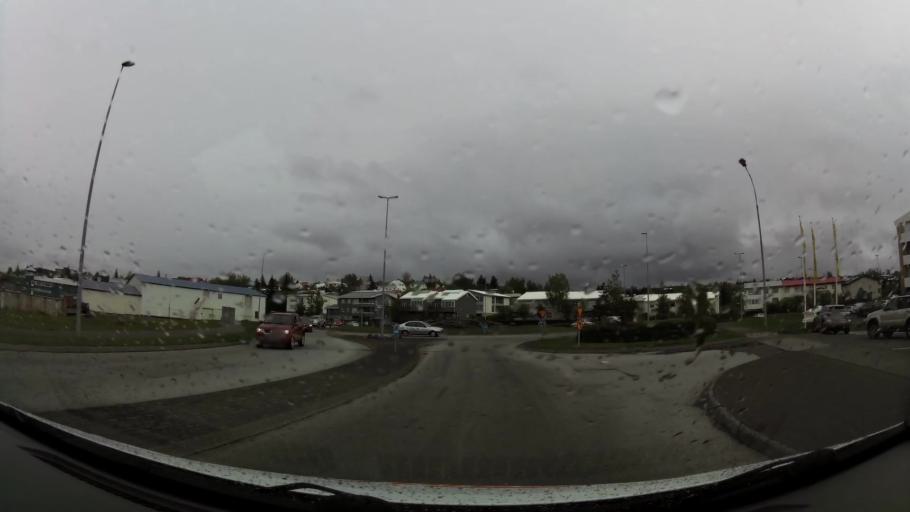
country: IS
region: Capital Region
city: Hafnarfjoerdur
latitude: 64.0623
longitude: -21.9638
